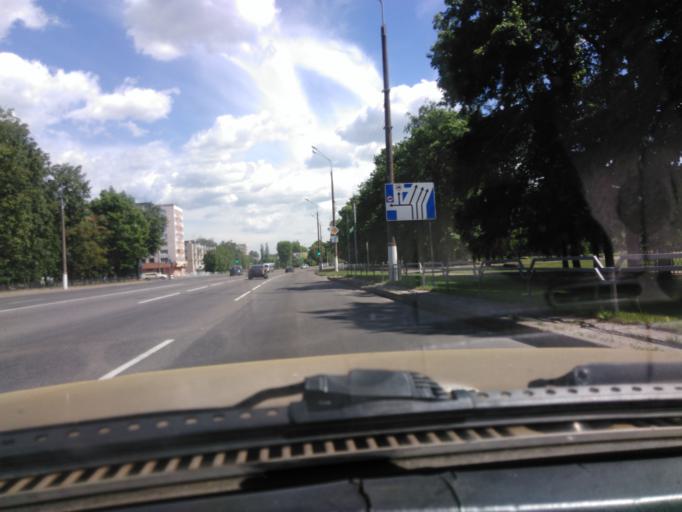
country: BY
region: Mogilev
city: Mahilyow
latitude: 53.9174
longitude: 30.3104
